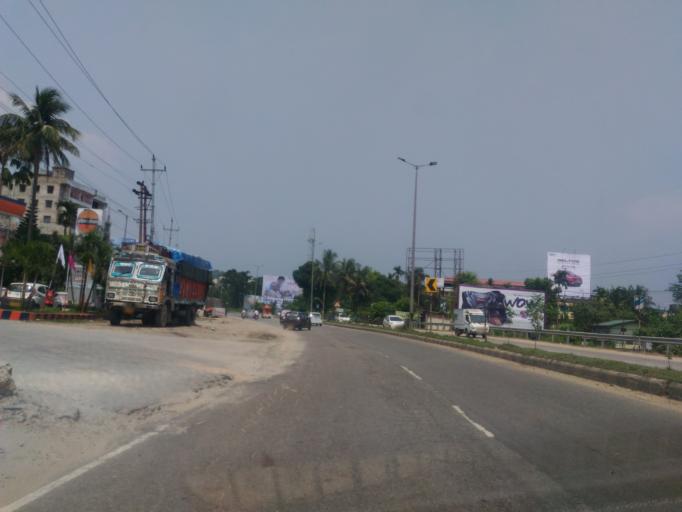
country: IN
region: Assam
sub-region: Kamrup
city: Soalkuchi
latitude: 26.1373
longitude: 91.6330
